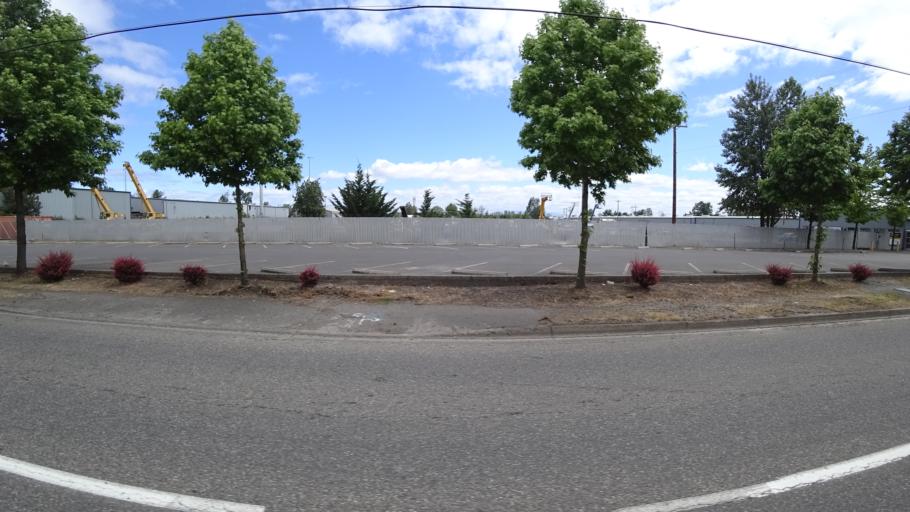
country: US
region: Oregon
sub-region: Washington County
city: West Haven
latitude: 45.6107
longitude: -122.7611
